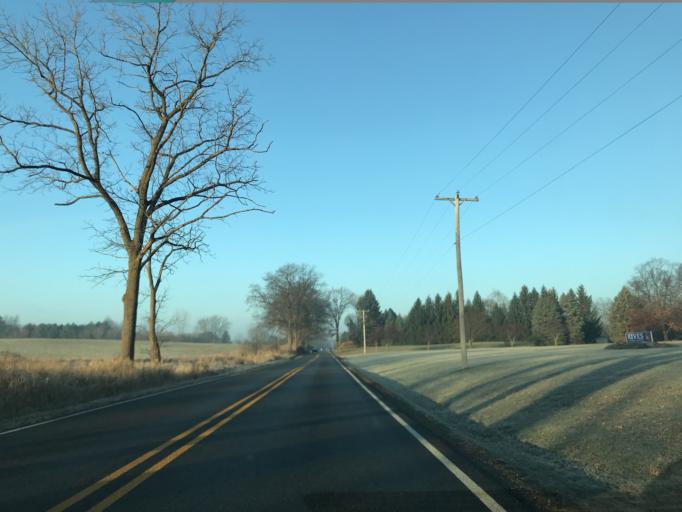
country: US
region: Michigan
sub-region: Ingham County
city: Leslie
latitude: 42.3787
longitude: -84.4383
